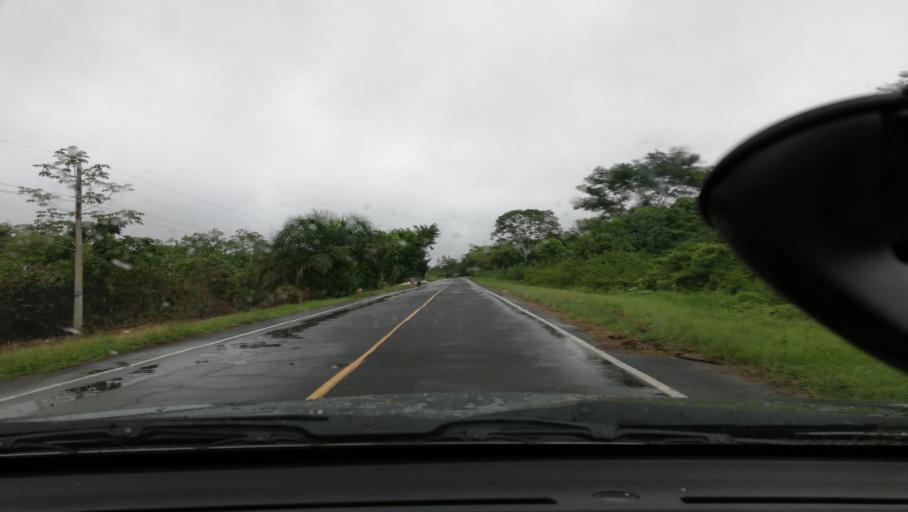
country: PE
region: Loreto
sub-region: Provincia de Maynas
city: San Juan
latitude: -4.1907
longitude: -73.4757
